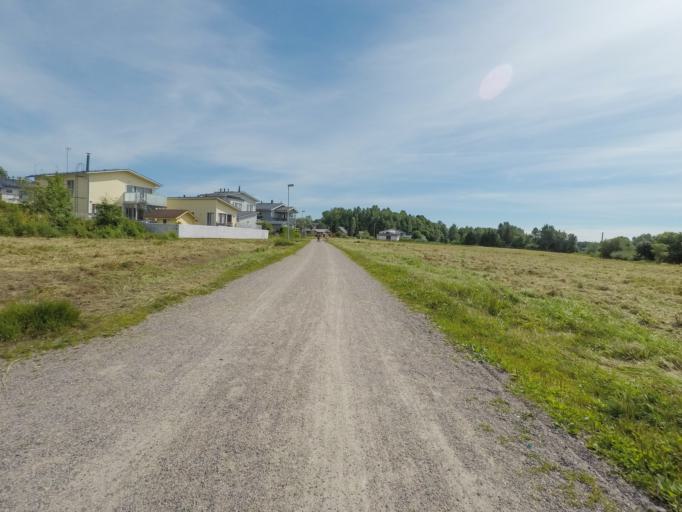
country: FI
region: Uusimaa
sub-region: Helsinki
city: Vantaa
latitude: 60.2613
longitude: 24.9755
